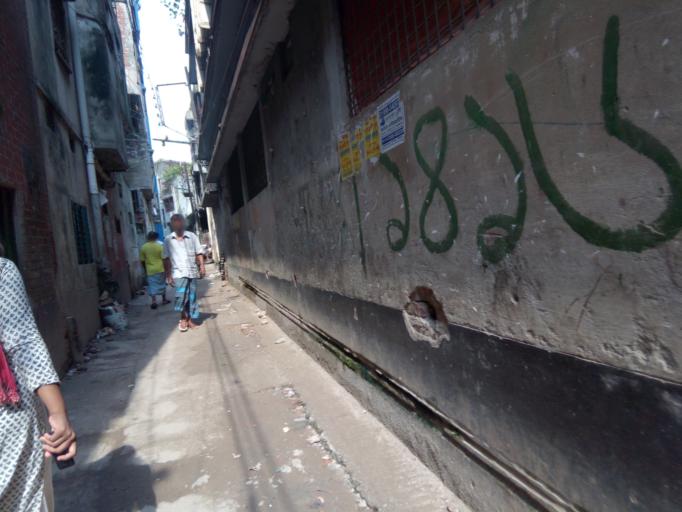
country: BD
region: Dhaka
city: Azimpur
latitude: 23.7391
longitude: 90.3639
